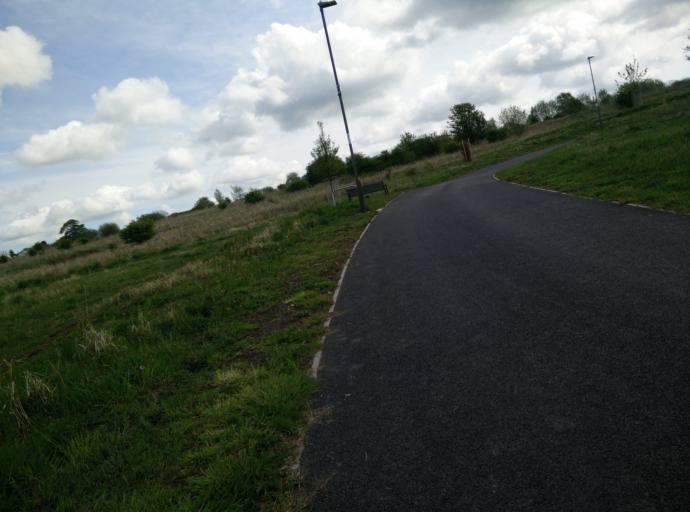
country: GB
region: Scotland
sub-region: Midlothian
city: Bonnyrigg
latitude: 55.9221
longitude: -3.1221
